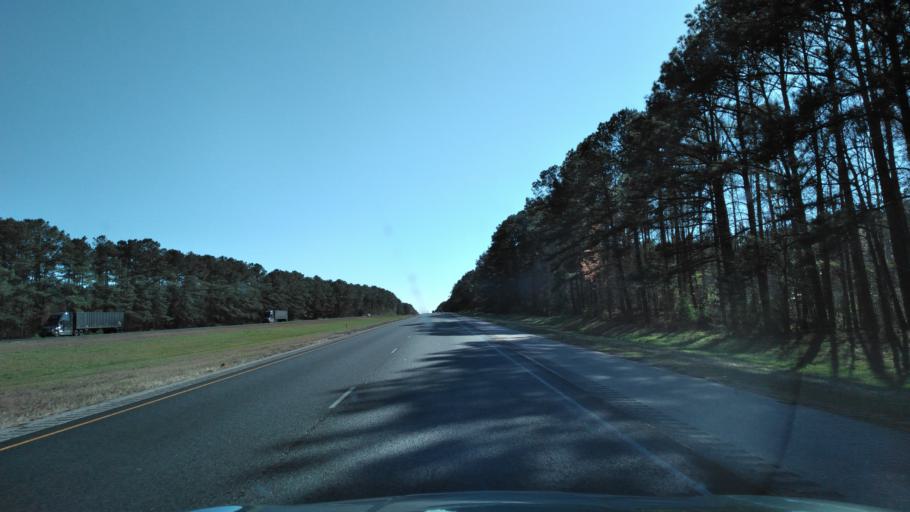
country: US
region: Alabama
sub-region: Butler County
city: Georgiana
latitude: 31.6929
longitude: -86.7466
